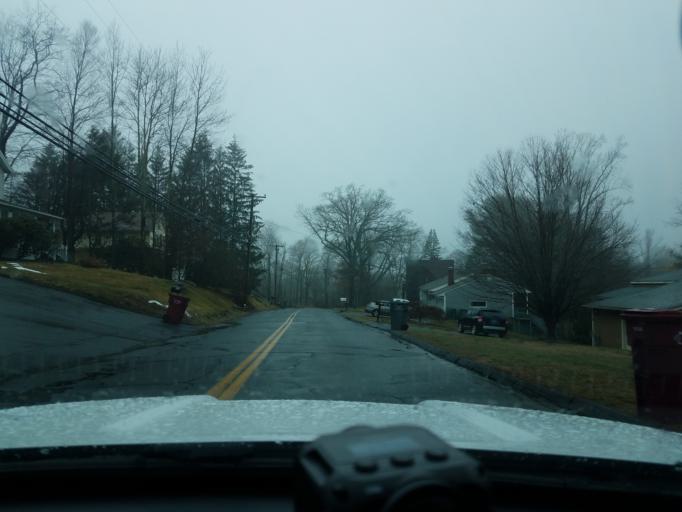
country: US
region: Connecticut
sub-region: New Haven County
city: Naugatuck
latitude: 41.4877
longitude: -73.0393
